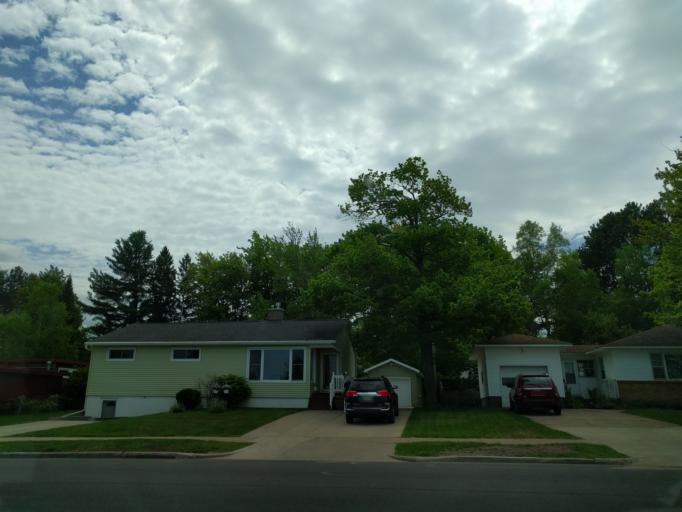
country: US
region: Michigan
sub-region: Marquette County
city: Marquette
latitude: 46.5568
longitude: -87.4073
